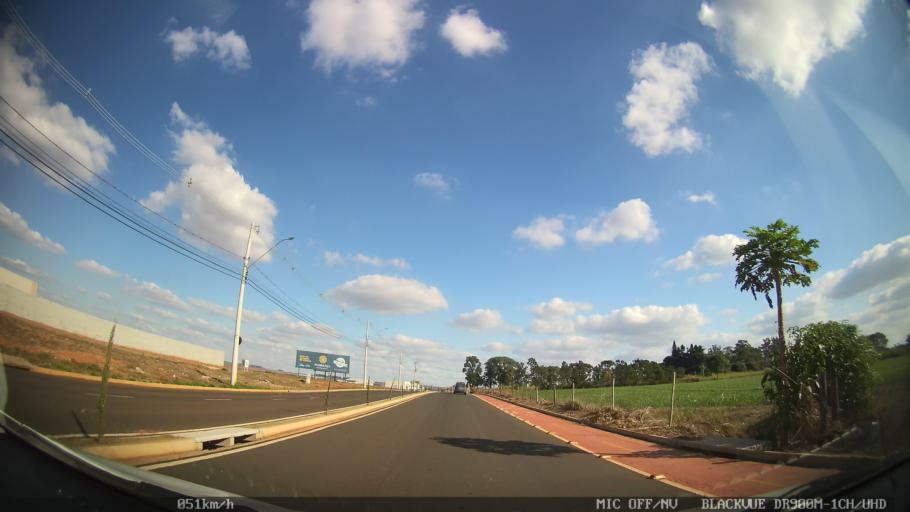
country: BR
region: Sao Paulo
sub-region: Nova Odessa
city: Nova Odessa
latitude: -22.8101
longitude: -47.3207
